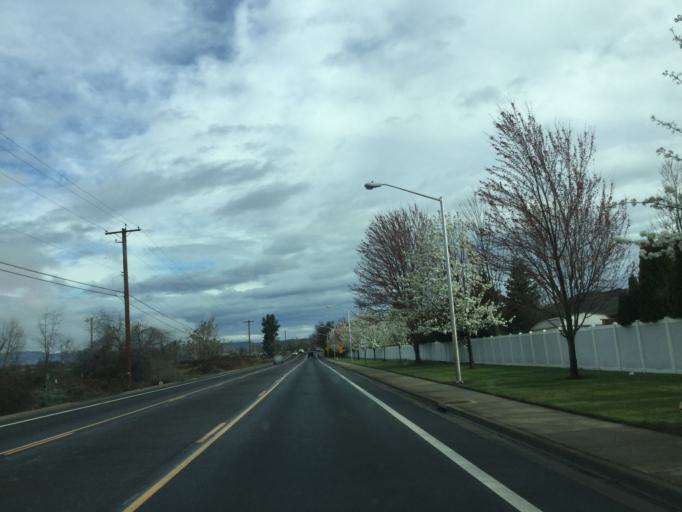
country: US
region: Oregon
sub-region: Jackson County
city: Central Point
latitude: 42.3833
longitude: -122.8930
